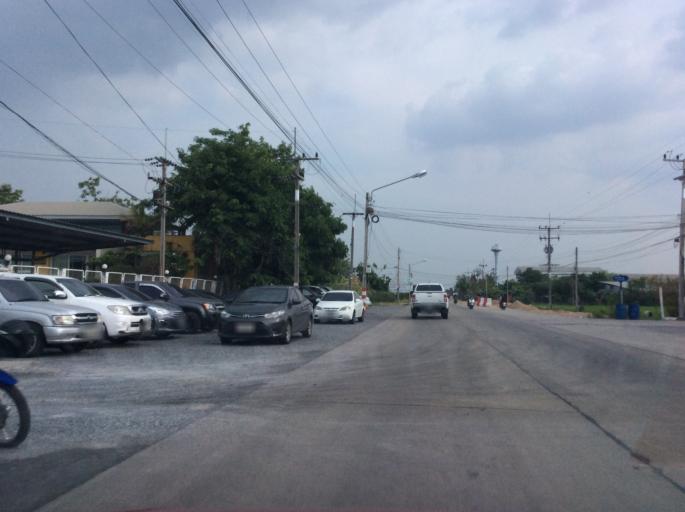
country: TH
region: Pathum Thani
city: Lam Luk Ka
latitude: 13.9677
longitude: 100.7260
